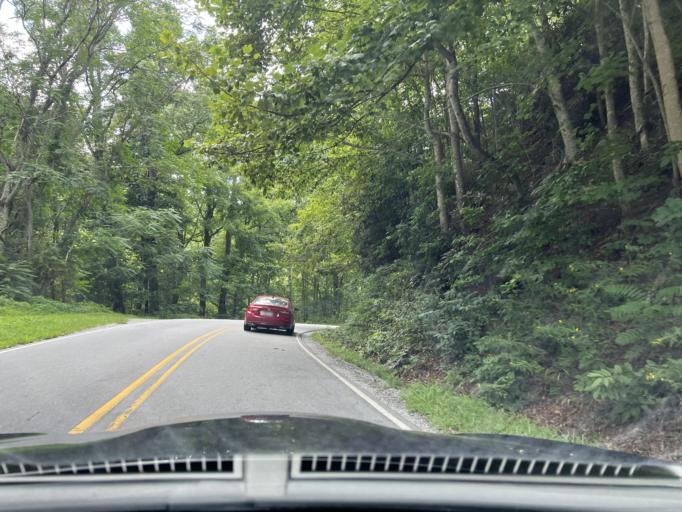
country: US
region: North Carolina
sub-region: Henderson County
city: Fruitland
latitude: 35.4186
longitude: -82.4142
